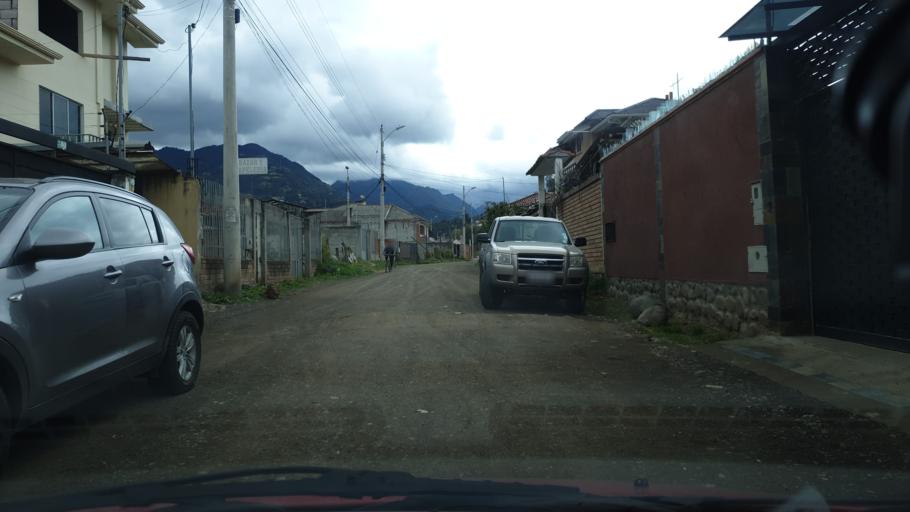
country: EC
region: Azuay
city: Cuenca
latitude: -2.8823
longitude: -79.0568
